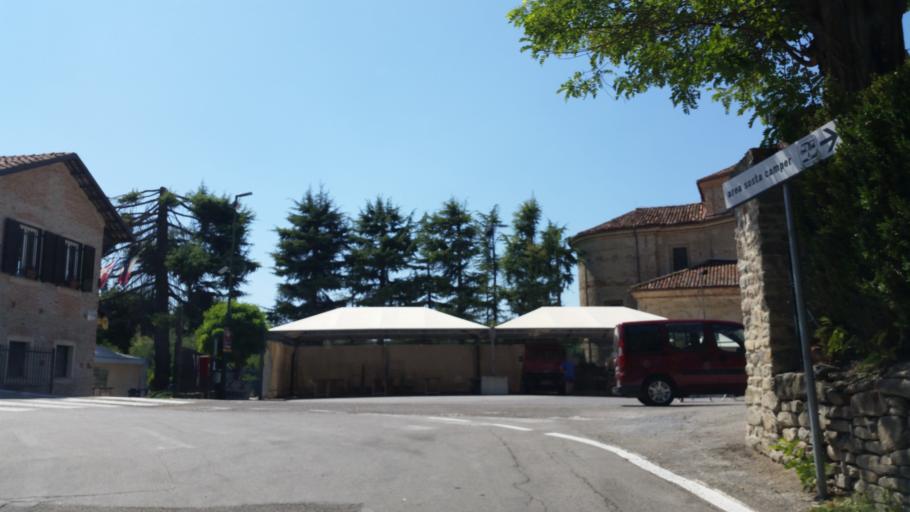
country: IT
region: Piedmont
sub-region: Provincia di Cuneo
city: Sinio
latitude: 44.5998
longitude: 8.0218
